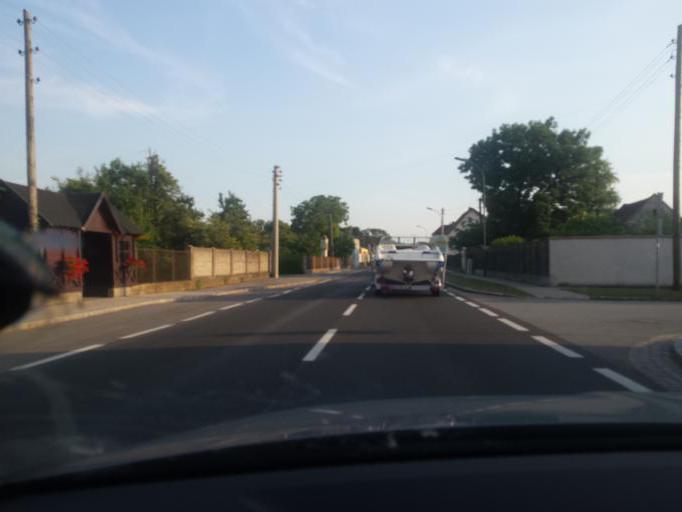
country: AT
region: Lower Austria
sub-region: Politischer Bezirk Bruck an der Leitha
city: Rohrau
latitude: 48.0578
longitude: 16.8449
